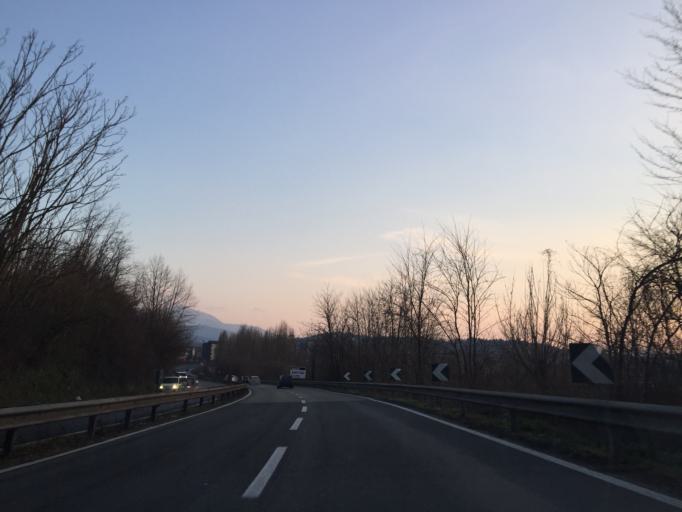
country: IT
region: Campania
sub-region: Provincia di Avellino
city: Atripalda
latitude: 40.9232
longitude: 14.8260
